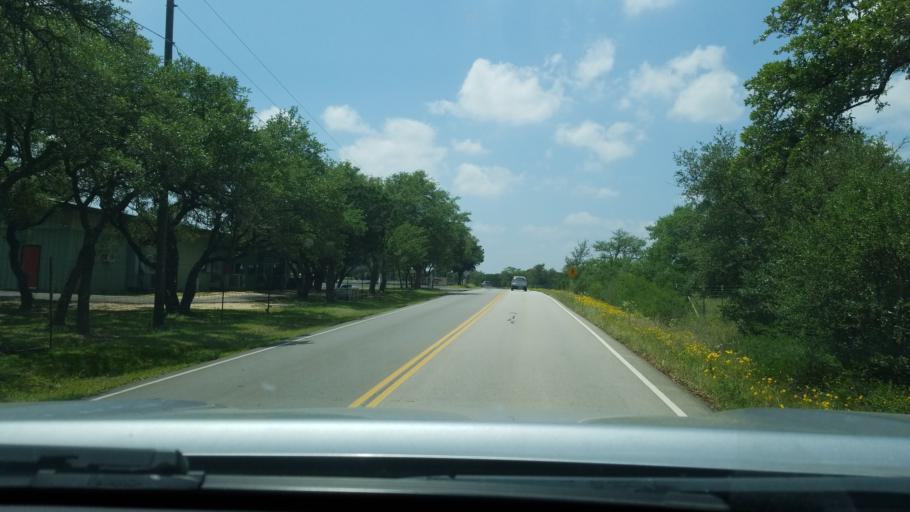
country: US
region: Texas
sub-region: Hays County
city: Woodcreek
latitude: 30.0429
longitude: -98.1079
